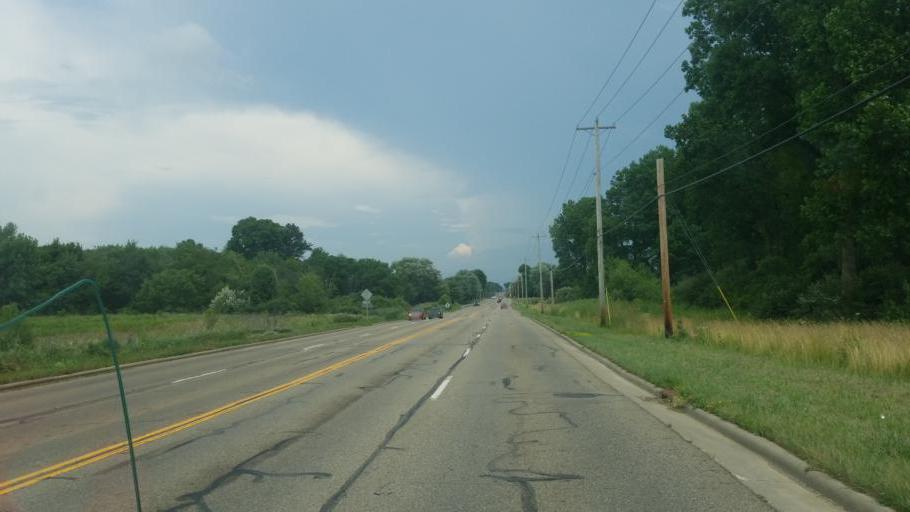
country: US
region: Ohio
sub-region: Stark County
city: North Canton
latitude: 40.8898
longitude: -81.3815
